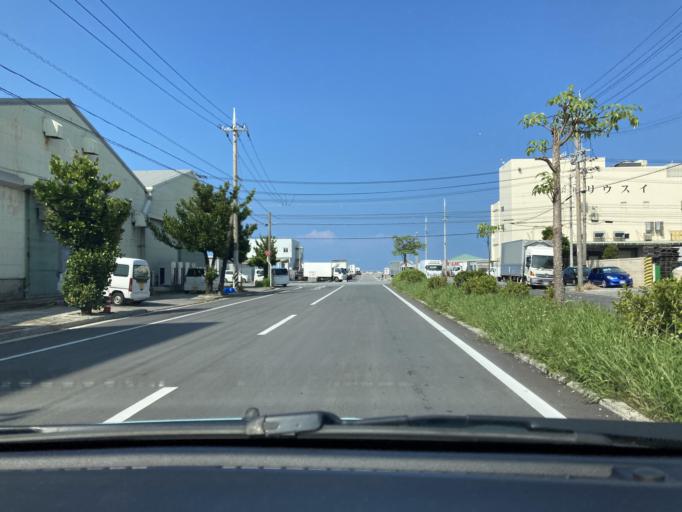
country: JP
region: Okinawa
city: Naha-shi
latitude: 26.2434
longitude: 127.6739
